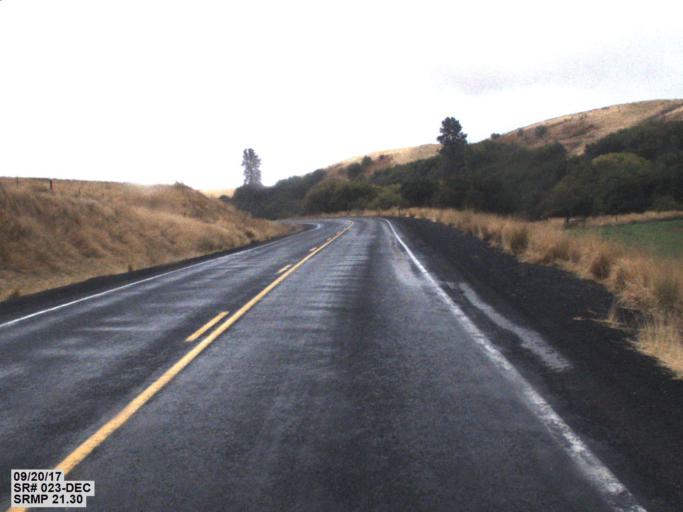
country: US
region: Washington
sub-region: Spokane County
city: Cheney
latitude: 47.1144
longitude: -117.7148
